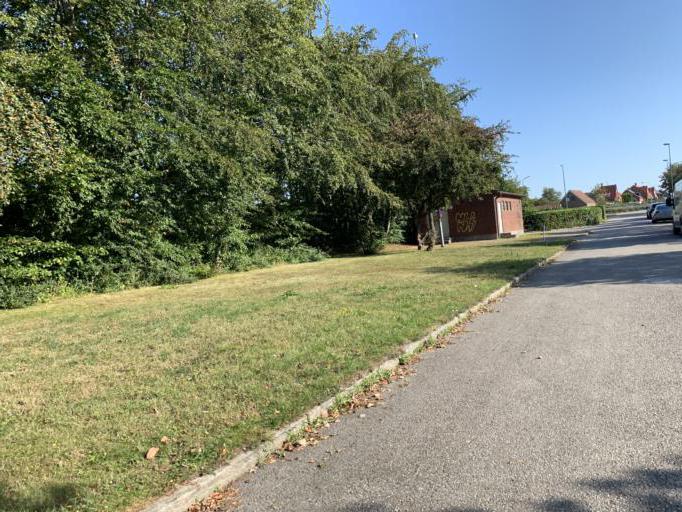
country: SE
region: Skane
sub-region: Trelleborgs Kommun
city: Trelleborg
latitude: 55.3685
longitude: 13.1784
